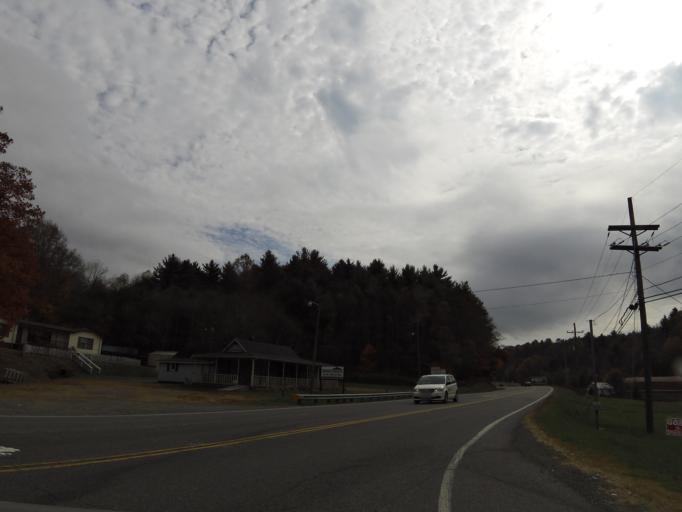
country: US
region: Virginia
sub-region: Carroll County
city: Hillsville
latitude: 36.6787
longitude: -80.6966
